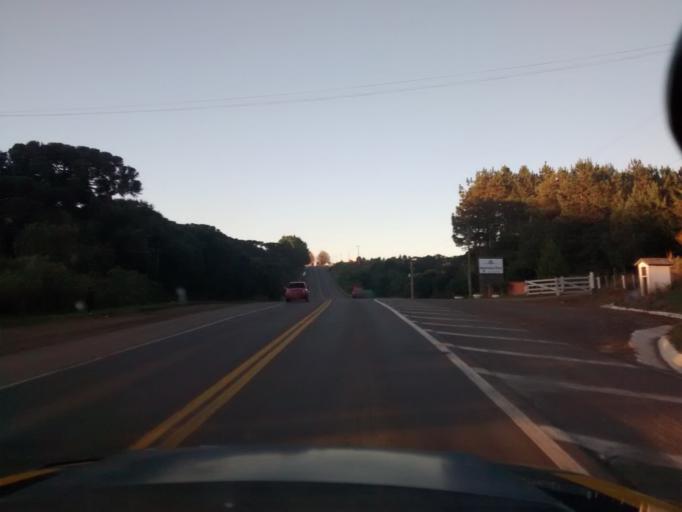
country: BR
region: Rio Grande do Sul
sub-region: Vacaria
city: Vacaria
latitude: -28.5291
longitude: -50.9513
